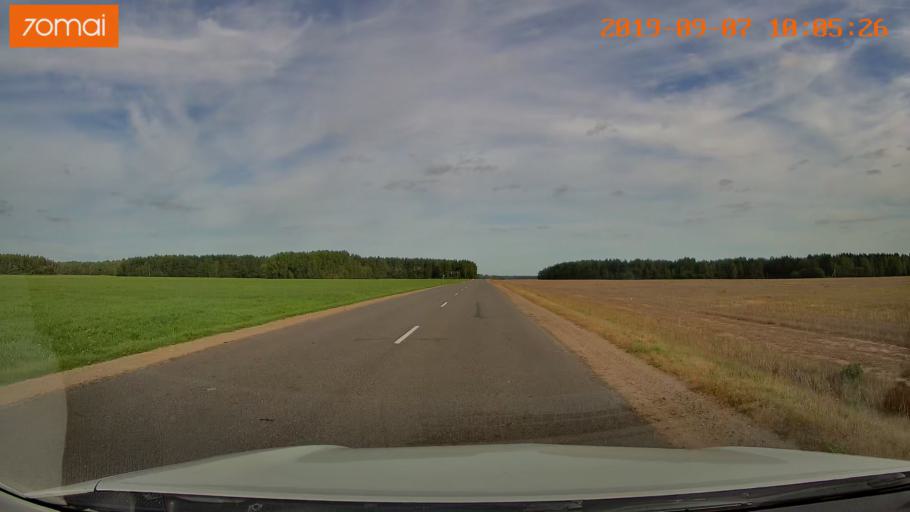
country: BY
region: Grodnenskaya
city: Voranava
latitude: 54.0473
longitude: 25.4074
